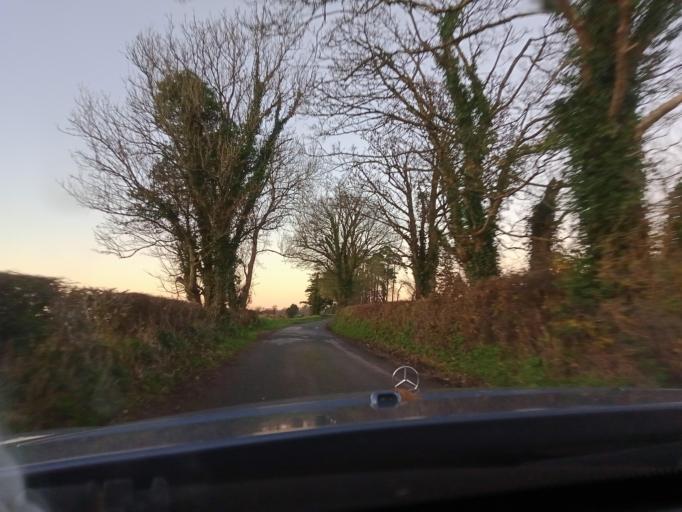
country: IE
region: Leinster
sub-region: Kilkenny
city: Thomastown
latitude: 52.4421
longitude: -7.1066
